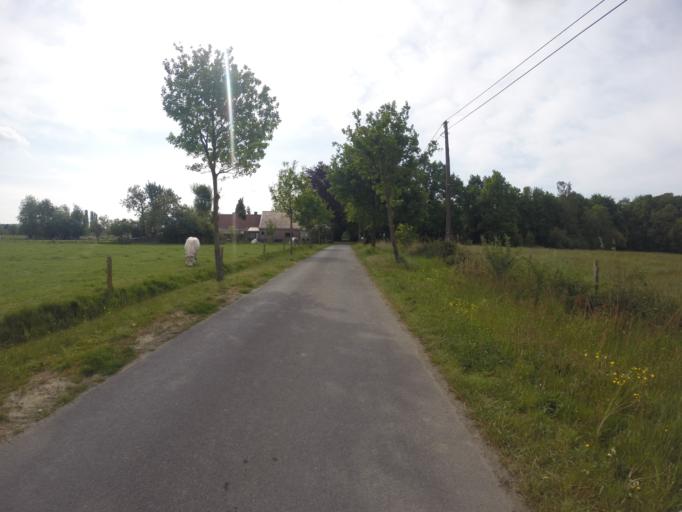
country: BE
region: Flanders
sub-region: Provincie West-Vlaanderen
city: Beernem
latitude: 51.0781
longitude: 3.3450
